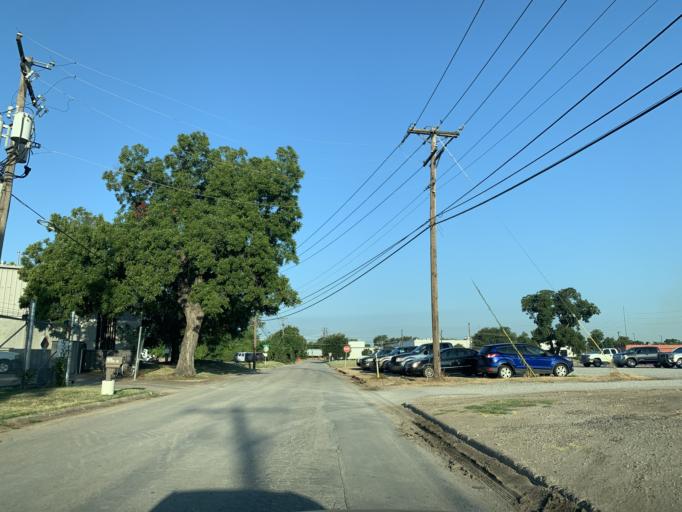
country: US
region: Texas
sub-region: Tarrant County
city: Fort Worth
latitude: 32.7569
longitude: -97.3461
